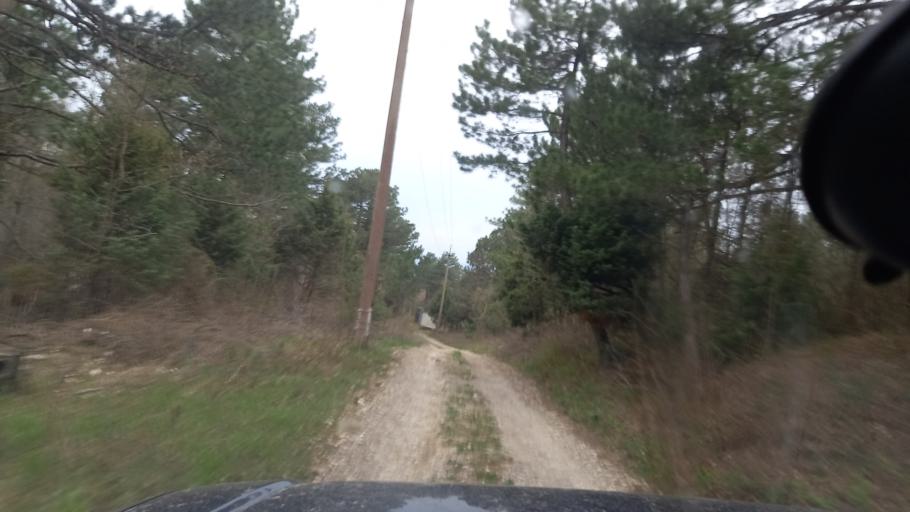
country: RU
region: Krasnodarskiy
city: Dzhubga
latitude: 44.3187
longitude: 38.6667
